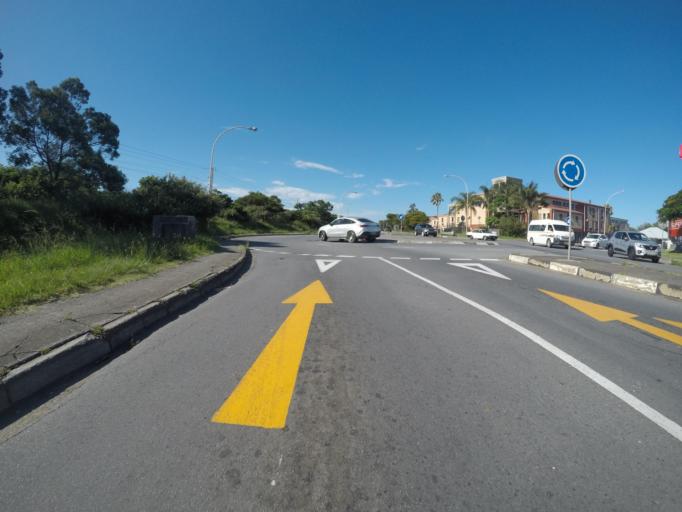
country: ZA
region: Eastern Cape
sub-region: Buffalo City Metropolitan Municipality
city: East London
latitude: -32.9827
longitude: 27.8982
